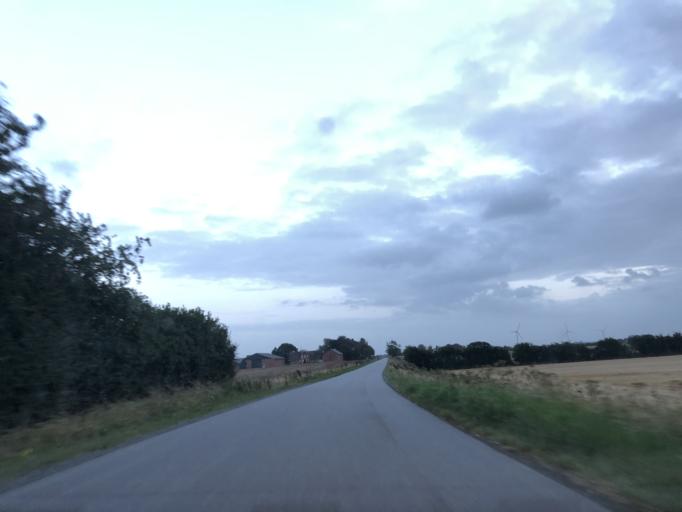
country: DK
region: South Denmark
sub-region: Haderslev Kommune
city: Starup
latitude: 55.2469
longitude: 9.6404
